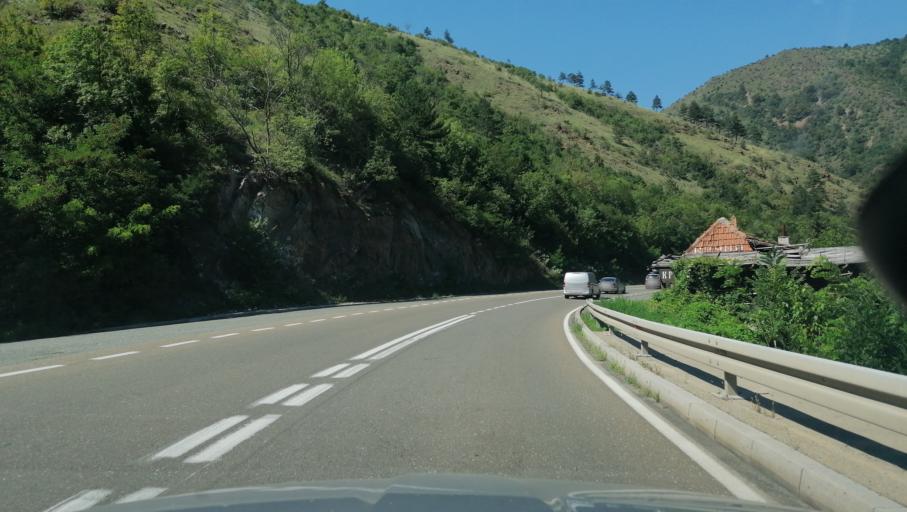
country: RS
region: Central Serbia
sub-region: Raski Okrug
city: Kraljevo
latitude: 43.5827
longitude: 20.5797
